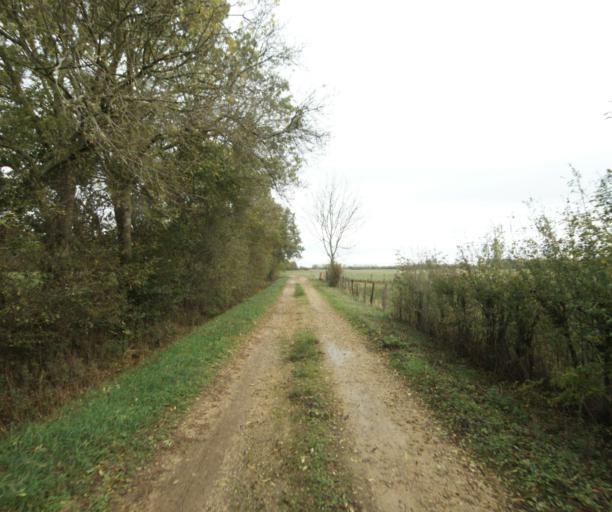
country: FR
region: Rhone-Alpes
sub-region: Departement de l'Ain
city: Pont-de-Vaux
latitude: 46.4543
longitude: 4.8964
